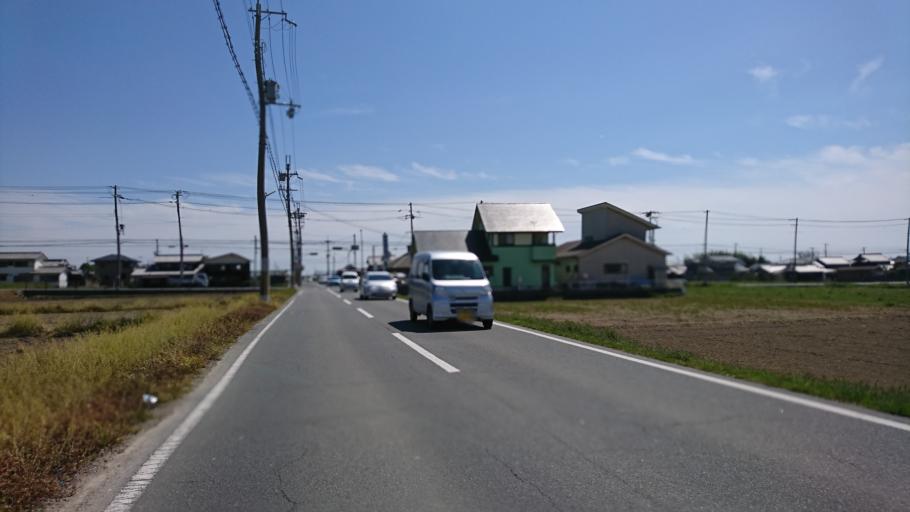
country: JP
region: Hyogo
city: Kakogawacho-honmachi
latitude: 34.7450
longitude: 134.8905
